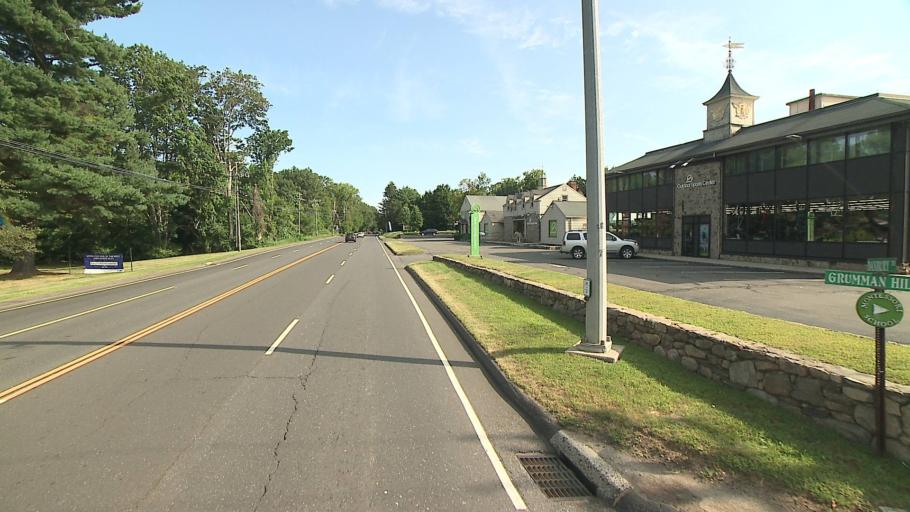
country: US
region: Connecticut
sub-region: Fairfield County
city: Wilton
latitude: 41.1703
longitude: -73.4163
